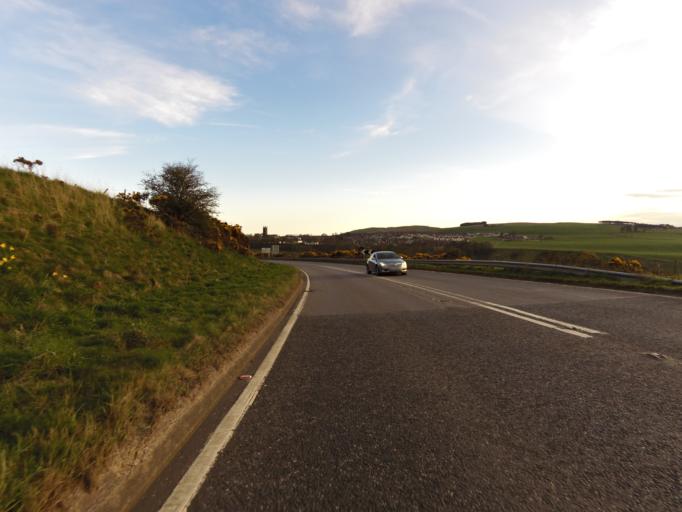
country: GB
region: Scotland
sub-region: Aberdeenshire
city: Inverbervie
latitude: 56.8501
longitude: -2.2791
